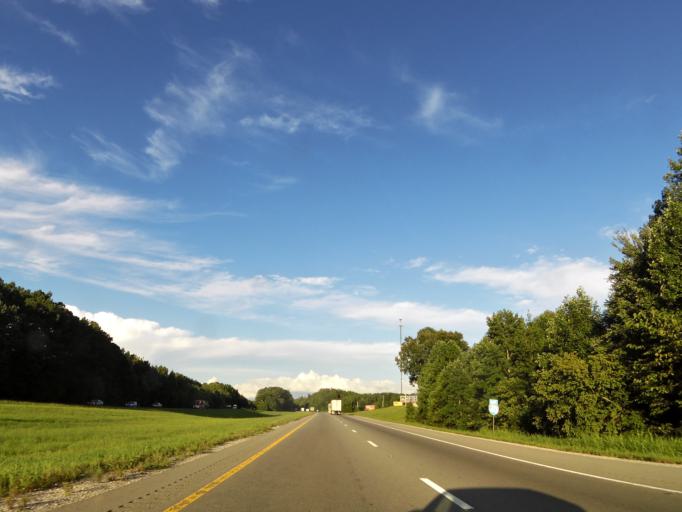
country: US
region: Tennessee
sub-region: Putnam County
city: Baxter
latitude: 36.1376
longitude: -85.6217
